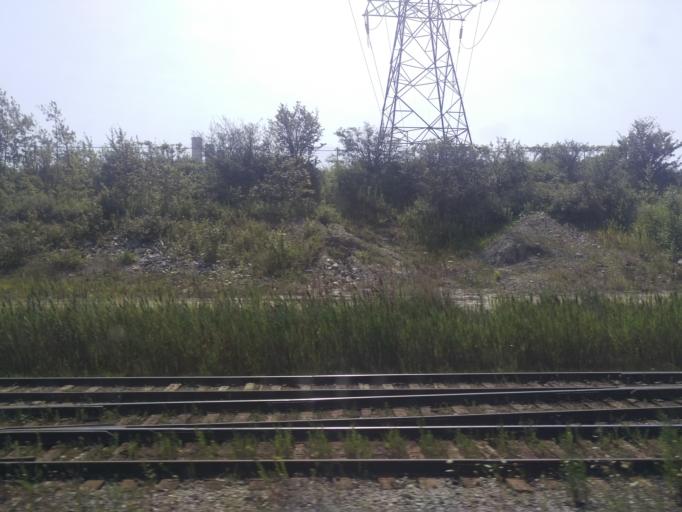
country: CA
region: Ontario
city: Oshawa
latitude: 43.8728
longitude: -78.8788
